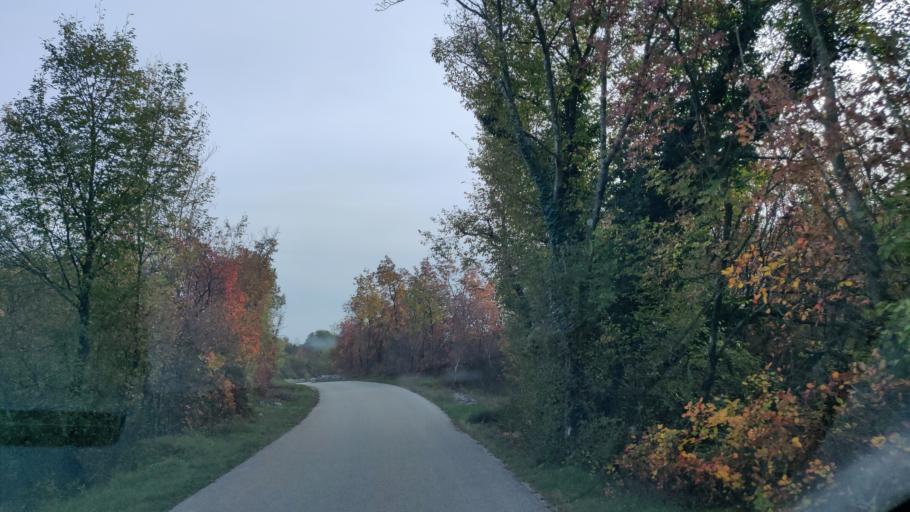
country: SI
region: Miren-Kostanjevica
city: Miren
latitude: 45.8559
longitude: 13.6052
